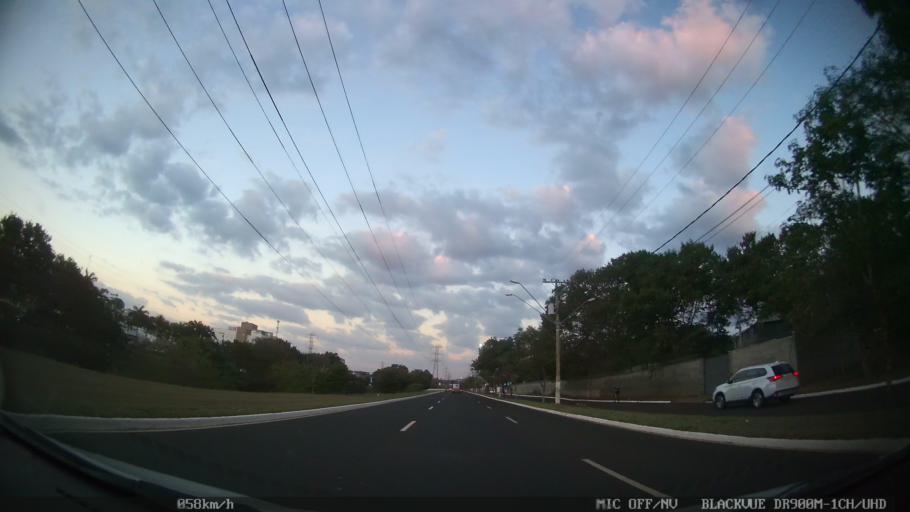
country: BR
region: Sao Paulo
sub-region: Ribeirao Preto
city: Ribeirao Preto
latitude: -21.2104
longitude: -47.7827
